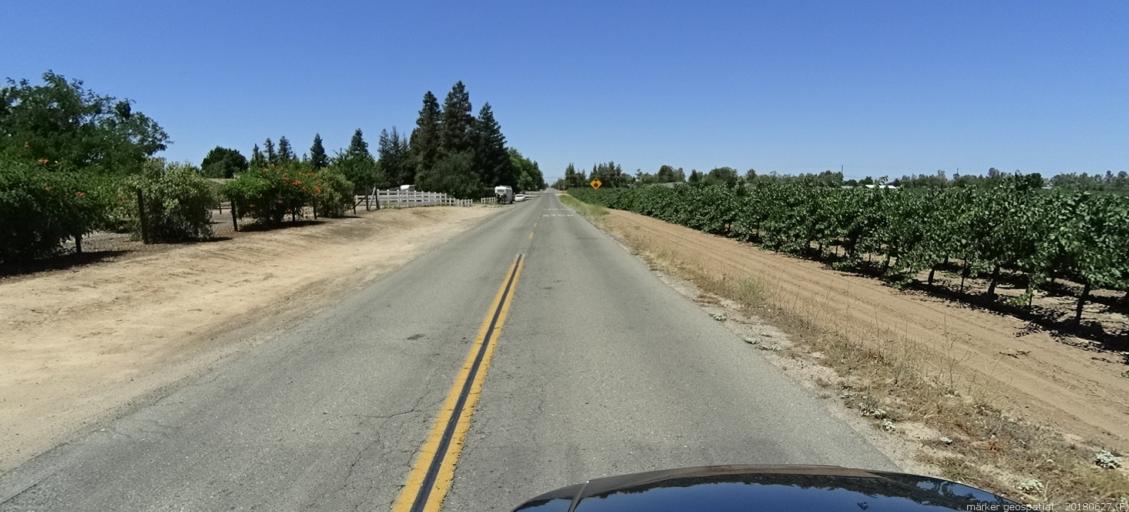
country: US
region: California
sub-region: Madera County
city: Bonadelle Ranchos-Madera Ranchos
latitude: 36.9375
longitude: -119.8916
